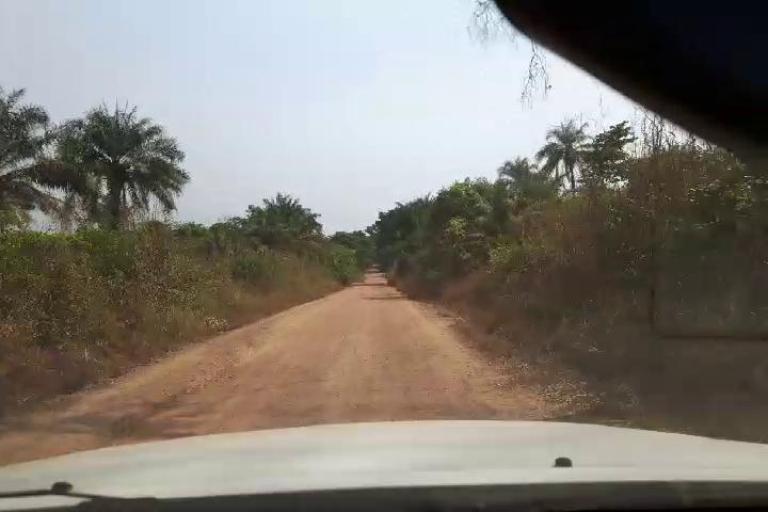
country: SL
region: Northern Province
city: Masingbi
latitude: 8.7922
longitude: -11.8693
